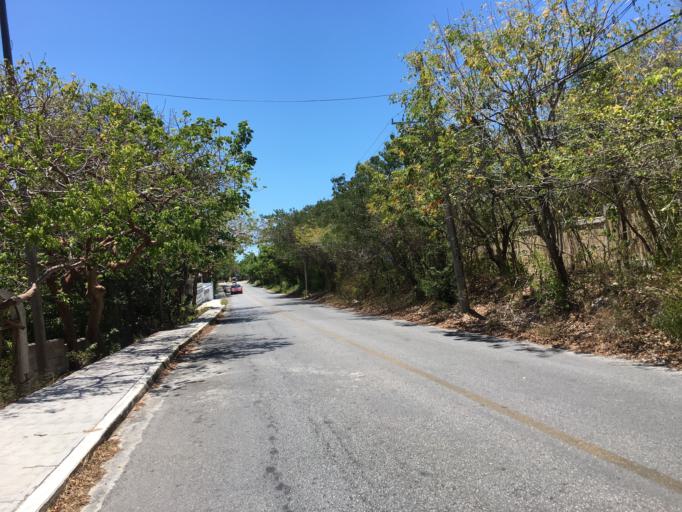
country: MX
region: Quintana Roo
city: Isla Mujeres
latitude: 21.2172
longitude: -86.7263
